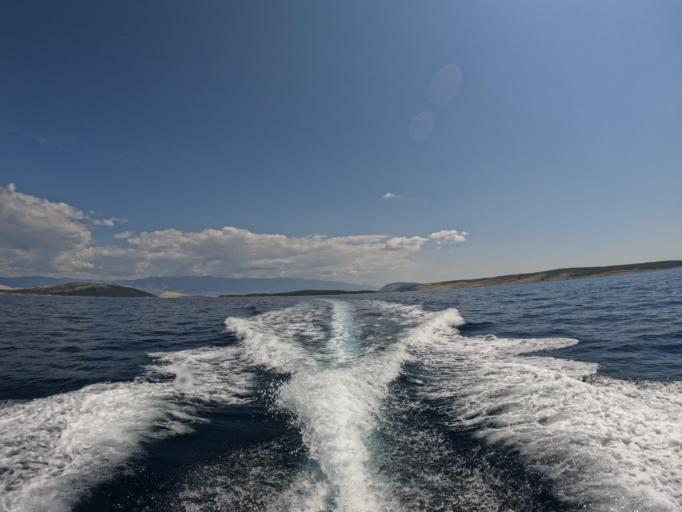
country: HR
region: Primorsko-Goranska
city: Lopar
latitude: 44.8626
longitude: 14.6910
